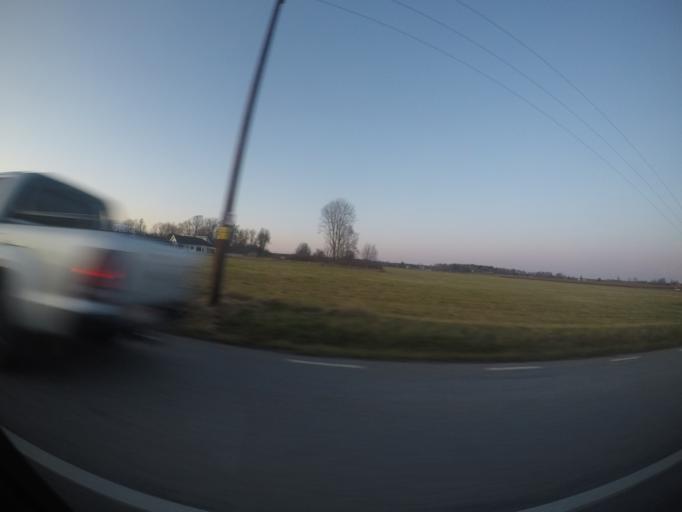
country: SE
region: OErebro
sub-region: Orebro Kommun
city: Hovsta
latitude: 59.3140
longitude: 15.3234
